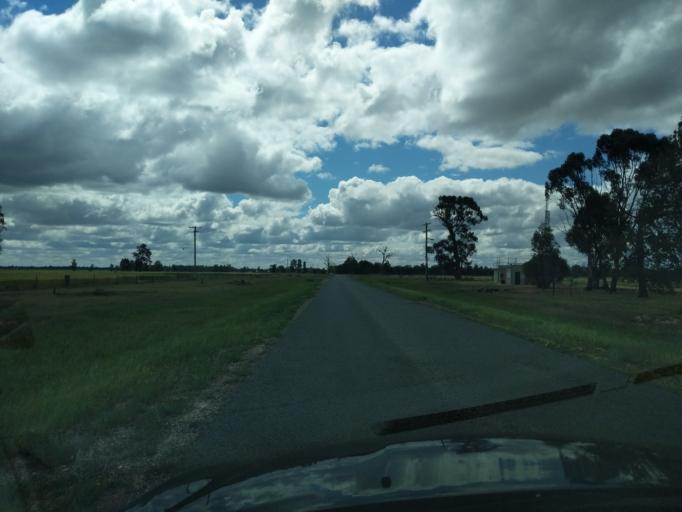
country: AU
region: New South Wales
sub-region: Coolamon
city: Coolamon
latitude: -34.8607
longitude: 146.8979
